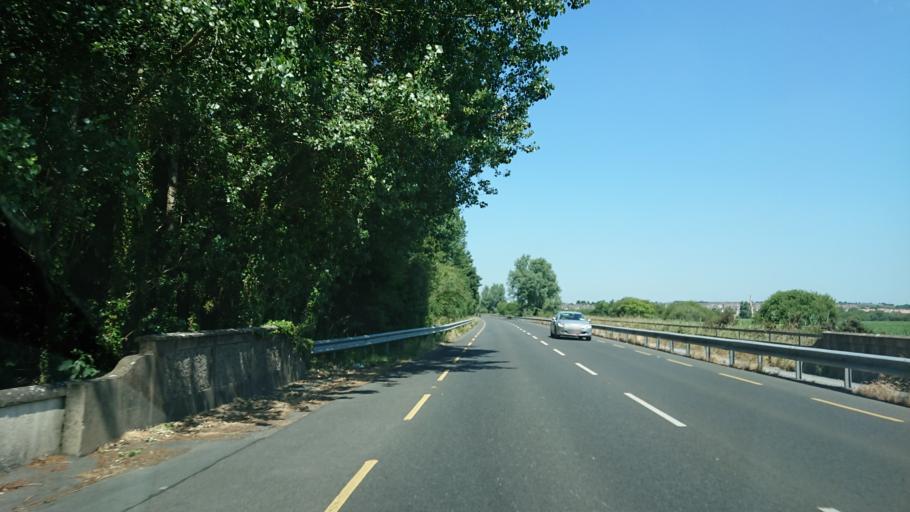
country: IE
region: Munster
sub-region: Waterford
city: Waterford
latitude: 52.2281
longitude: -7.1238
